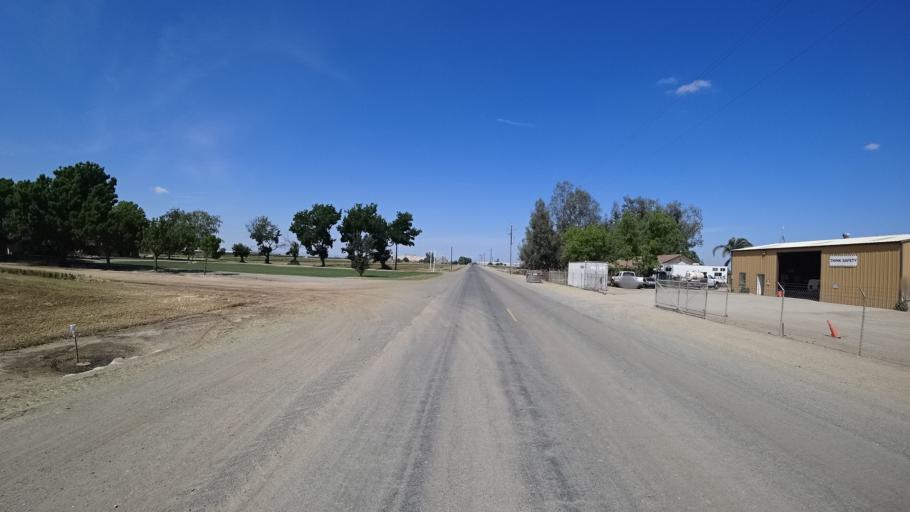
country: US
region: California
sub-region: Kings County
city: Home Garden
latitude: 36.2695
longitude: -119.6317
